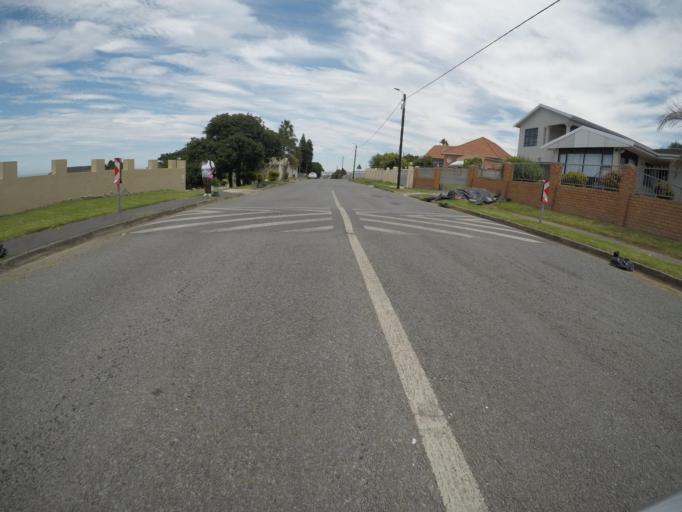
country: ZA
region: Eastern Cape
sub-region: Buffalo City Metropolitan Municipality
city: East London
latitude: -33.0392
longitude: 27.8543
